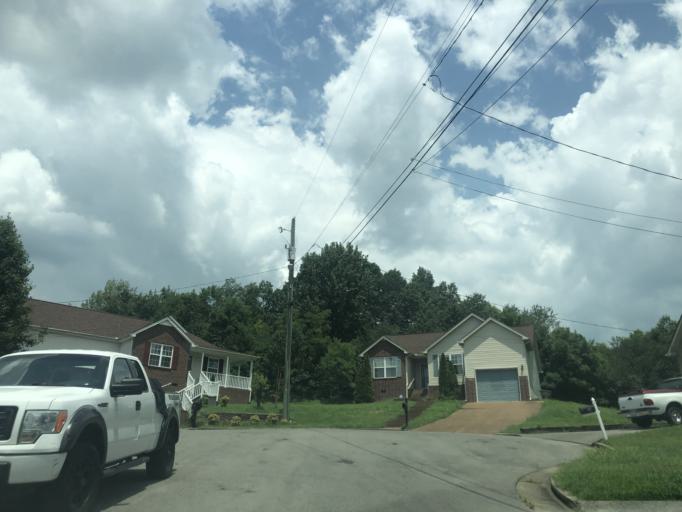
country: US
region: Tennessee
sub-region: Rutherford County
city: La Vergne
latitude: 36.0594
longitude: -86.6549
